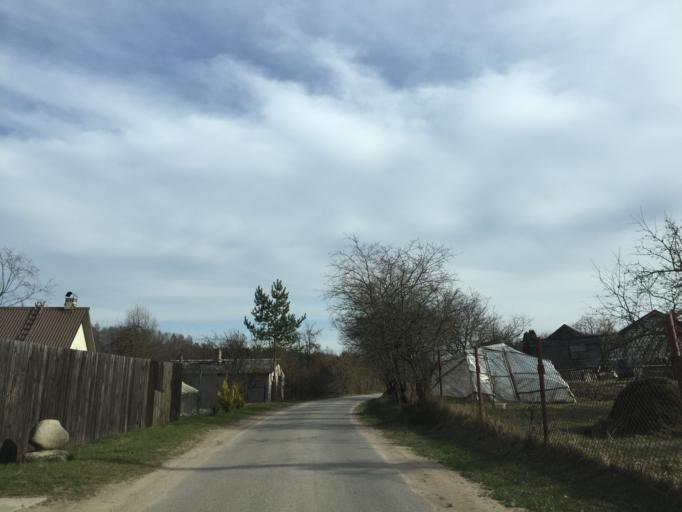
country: LV
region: Ogre
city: Ogre
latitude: 56.8088
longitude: 24.6369
